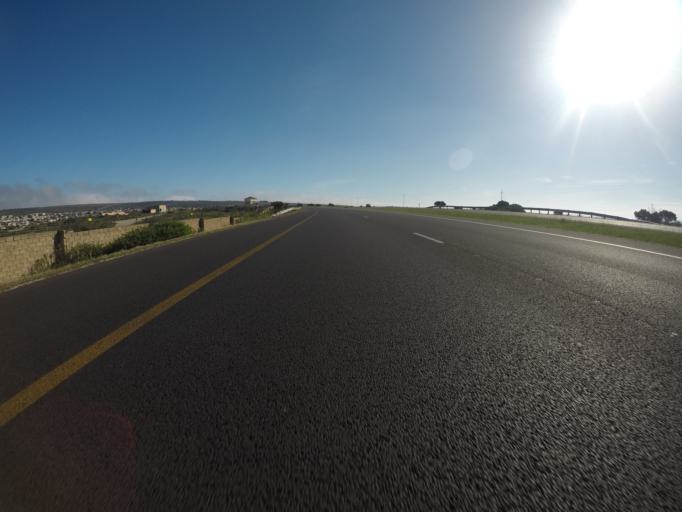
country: ZA
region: Western Cape
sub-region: Eden District Municipality
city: Mossel Bay
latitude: -34.1730
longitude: 22.0698
